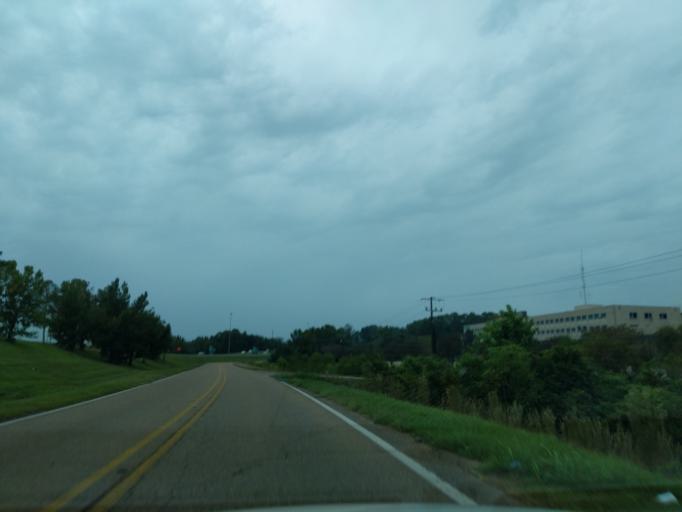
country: US
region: Mississippi
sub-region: Warren County
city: Vicksburg
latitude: 32.3199
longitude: -90.8796
